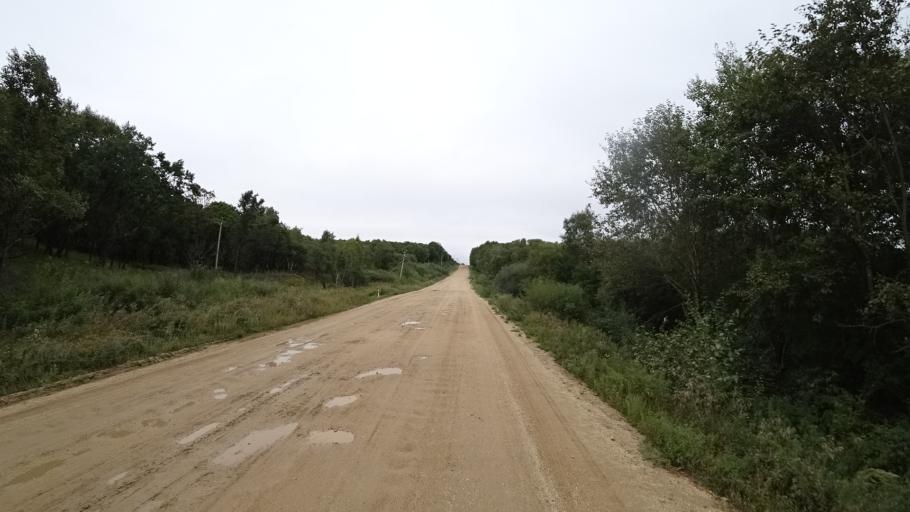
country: RU
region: Primorskiy
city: Ivanovka
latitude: 44.0724
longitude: 132.5823
